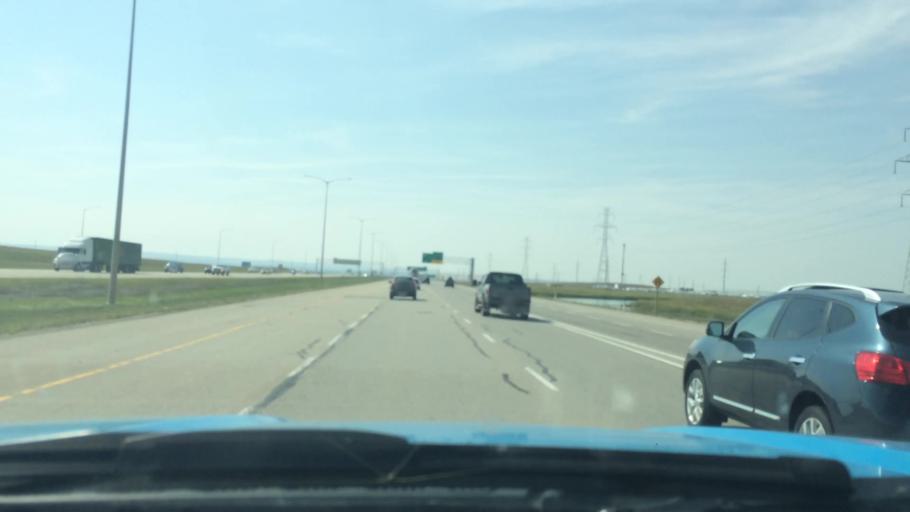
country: CA
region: Alberta
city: Airdrie
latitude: 51.1760
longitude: -113.9721
